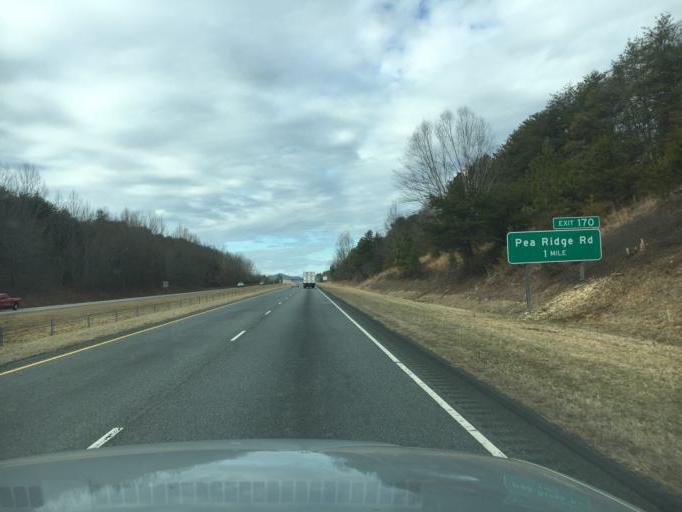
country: US
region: North Carolina
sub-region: Rutherford County
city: Rutherfordton
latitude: 35.2855
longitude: -82.0515
